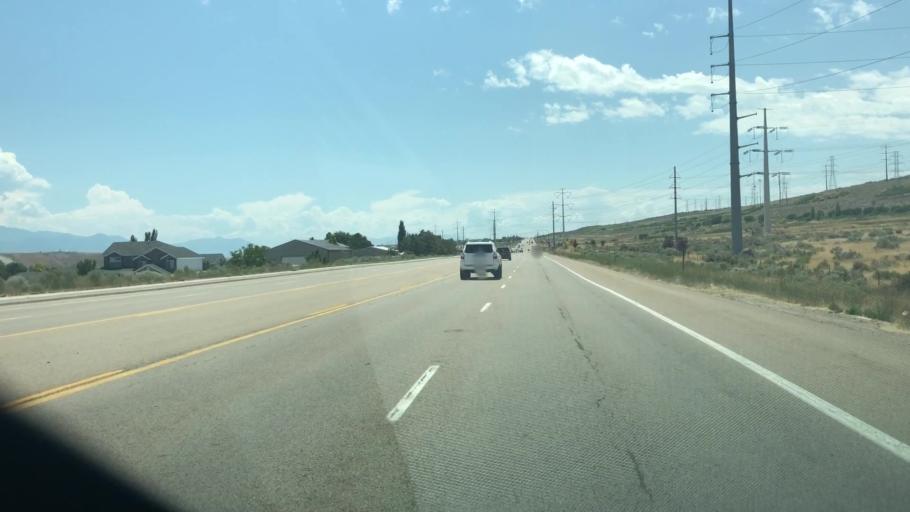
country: US
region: Utah
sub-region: Salt Lake County
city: Bluffdale
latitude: 40.5022
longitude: -111.9335
